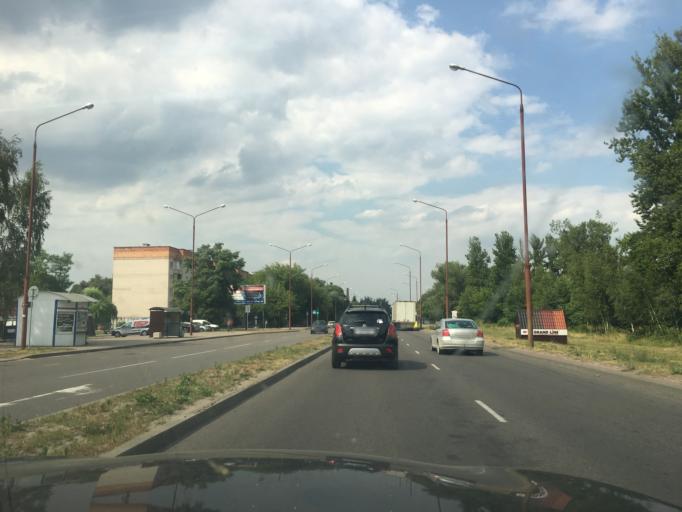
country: BY
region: Brest
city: Brest
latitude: 52.1352
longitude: 23.6754
